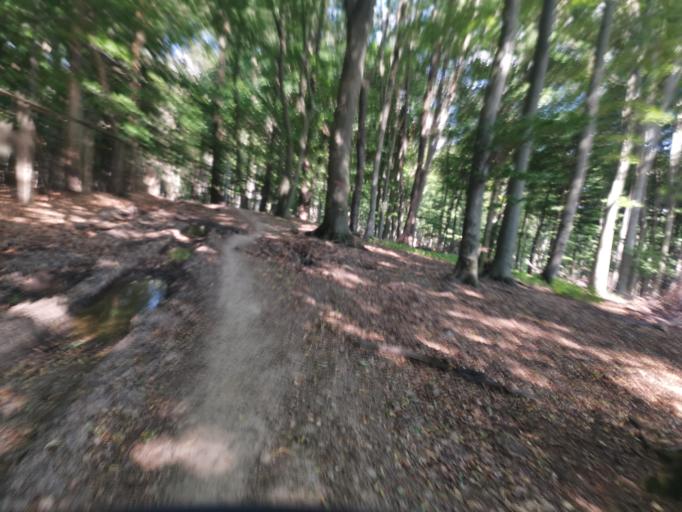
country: CZ
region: South Moravian
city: Knezdub
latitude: 48.8209
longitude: 17.4040
